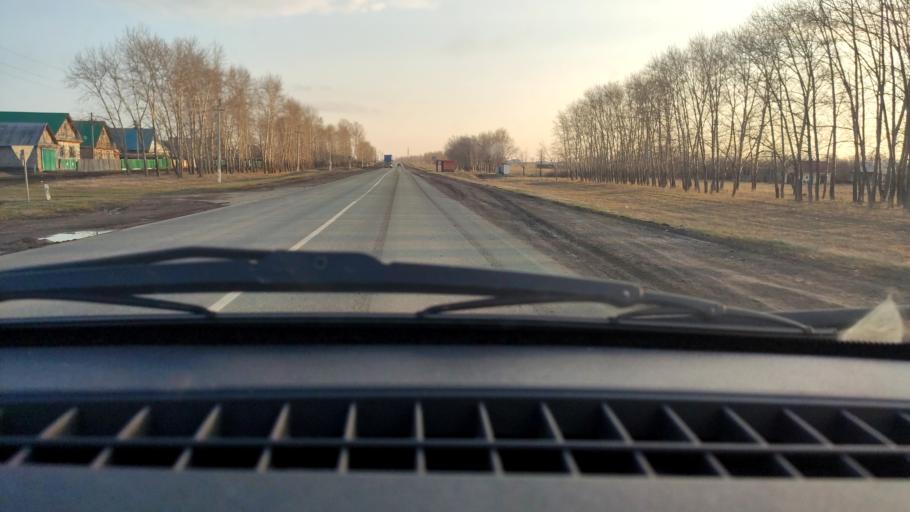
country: RU
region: Bashkortostan
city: Davlekanovo
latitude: 54.3922
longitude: 55.2043
